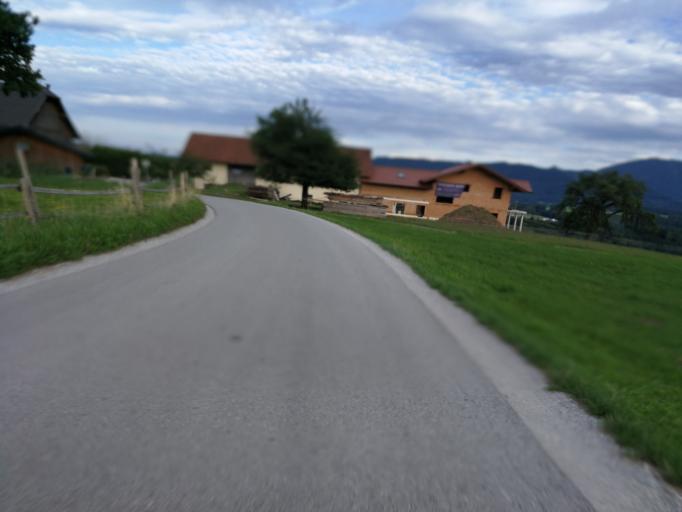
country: AT
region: Salzburg
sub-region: Politischer Bezirk Salzburg-Umgebung
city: Elixhausen
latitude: 47.8687
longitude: 13.0492
